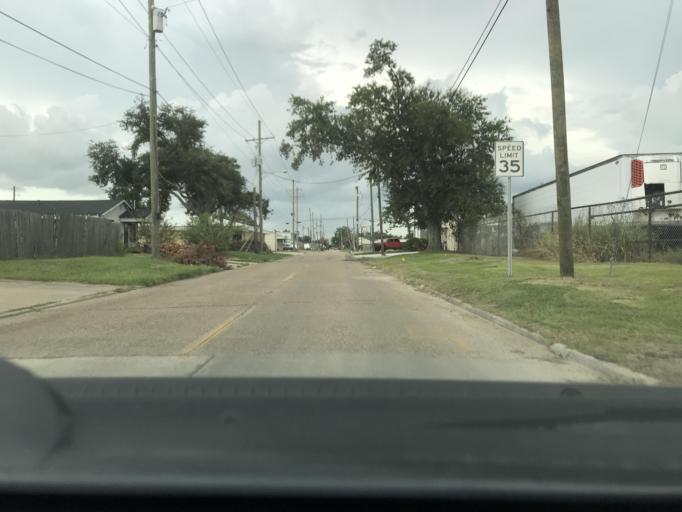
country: US
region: Louisiana
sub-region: Calcasieu Parish
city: Lake Charles
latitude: 30.2103
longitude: -93.2160
